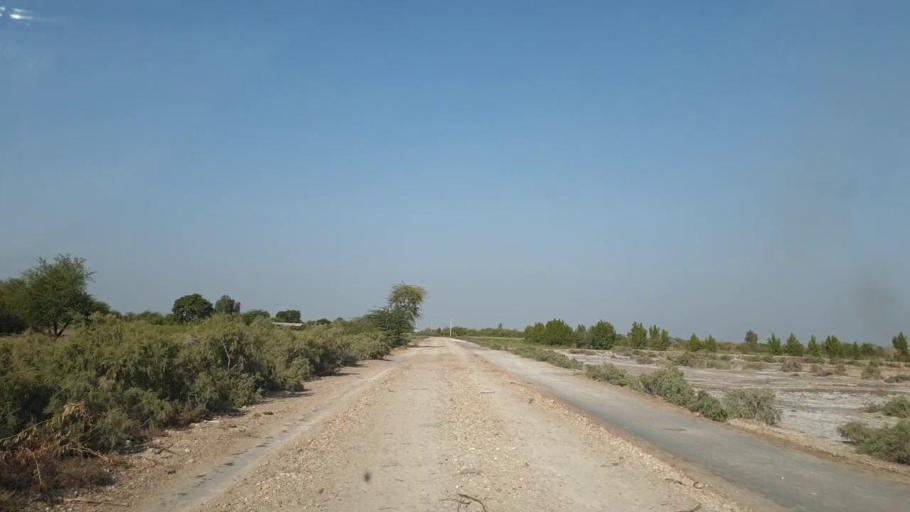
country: PK
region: Sindh
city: Tando Mittha Khan
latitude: 25.7464
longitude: 69.1951
